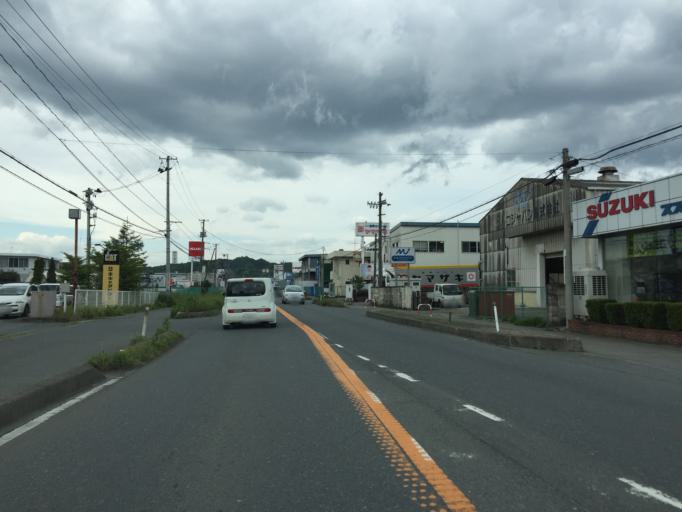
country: JP
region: Fukushima
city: Iwaki
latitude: 36.9774
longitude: 140.8700
